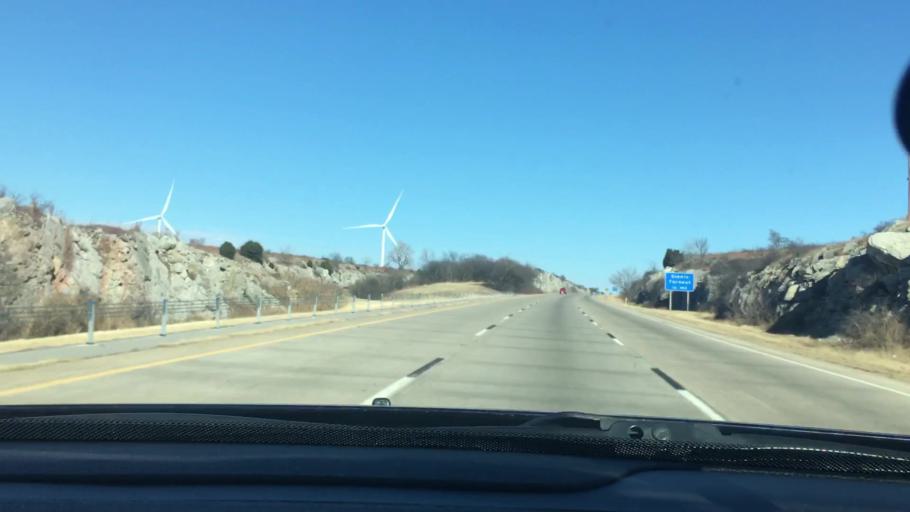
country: US
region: Oklahoma
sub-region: Murray County
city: Davis
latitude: 34.3693
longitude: -97.1458
